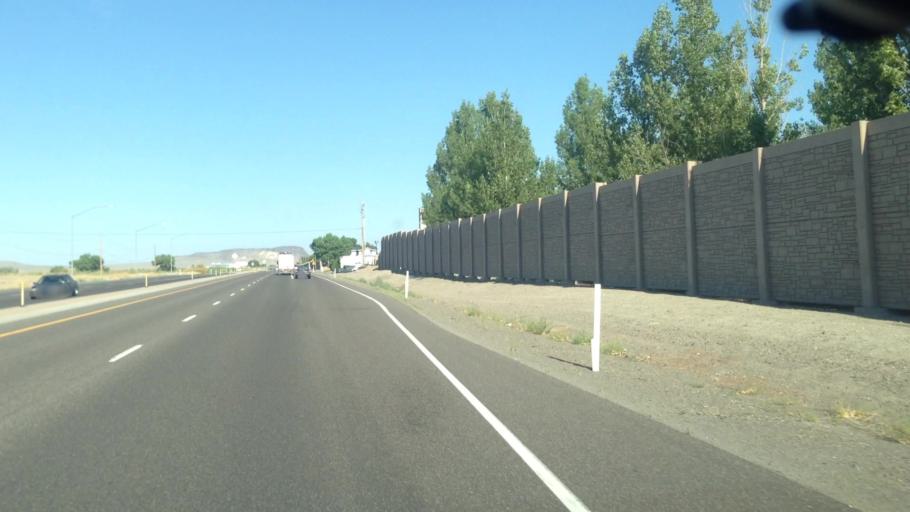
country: US
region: Nevada
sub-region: Lyon County
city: Fernley
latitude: 39.5930
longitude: -119.1580
